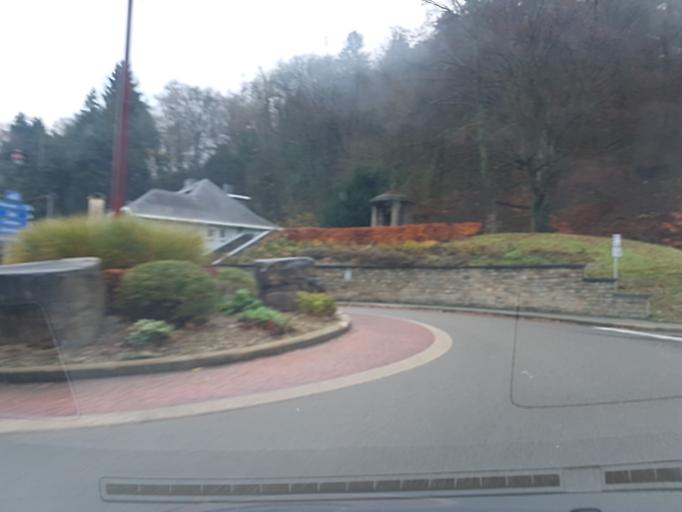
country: BE
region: Wallonia
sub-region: Province de Liege
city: Trooz
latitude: 50.5729
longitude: 5.6894
